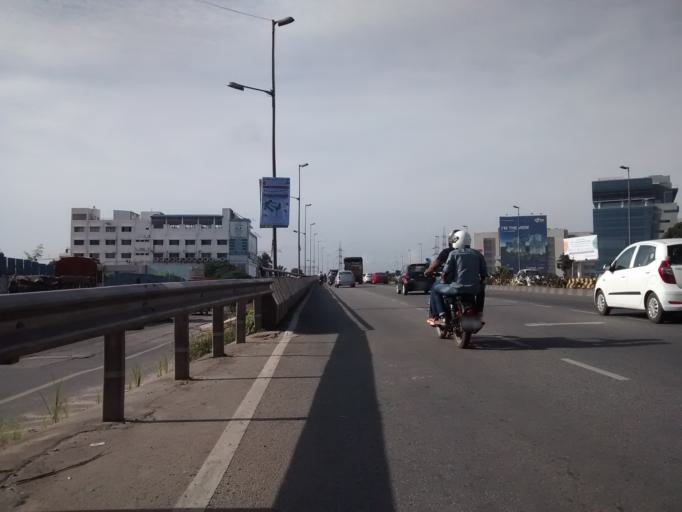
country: IN
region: Karnataka
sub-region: Bangalore Urban
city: Yelahanka
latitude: 13.0538
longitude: 77.5935
